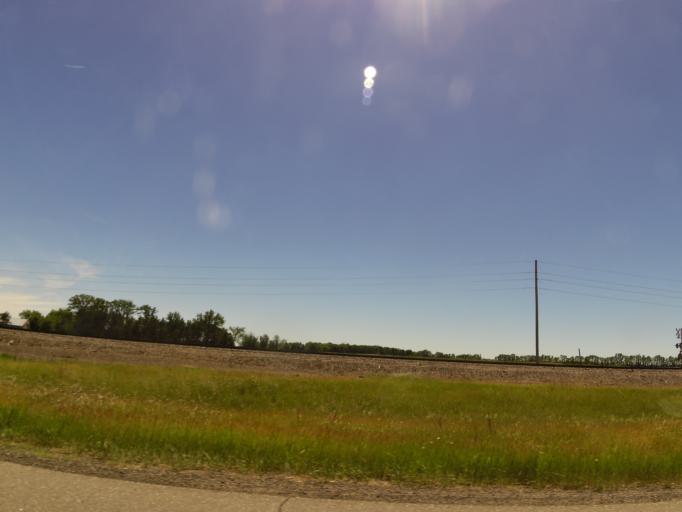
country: US
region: Minnesota
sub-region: Wadena County
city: Wadena
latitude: 46.4189
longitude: -95.0715
